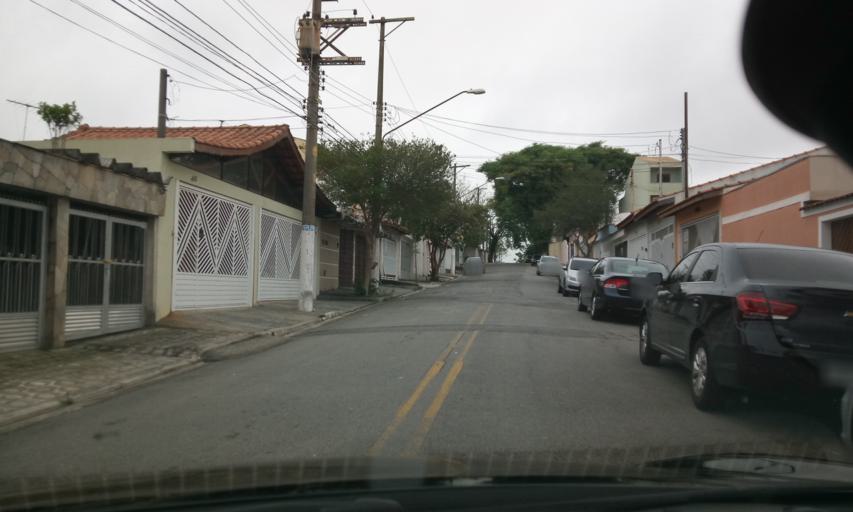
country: BR
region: Sao Paulo
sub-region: Sao Bernardo Do Campo
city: Sao Bernardo do Campo
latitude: -23.6757
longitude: -46.5655
